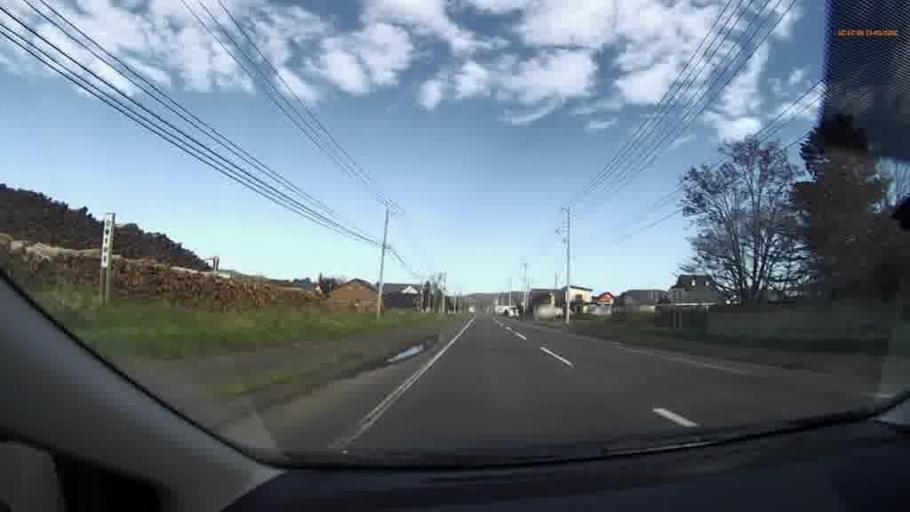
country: JP
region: Hokkaido
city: Kushiro
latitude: 42.9679
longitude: 144.0700
